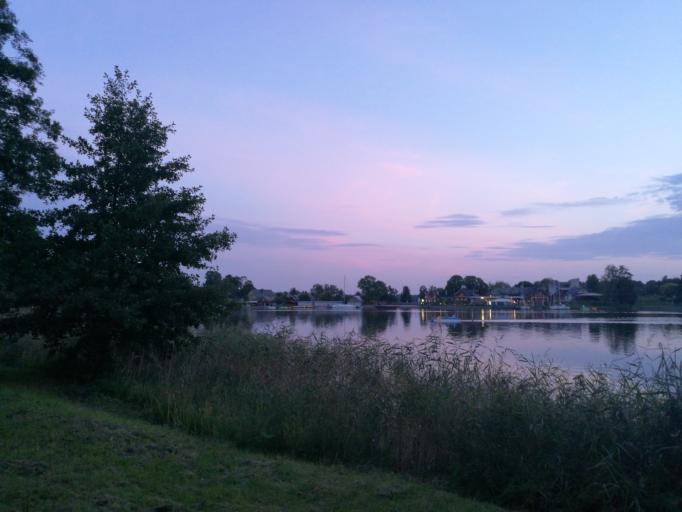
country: LT
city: Trakai
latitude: 54.6521
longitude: 24.9326
